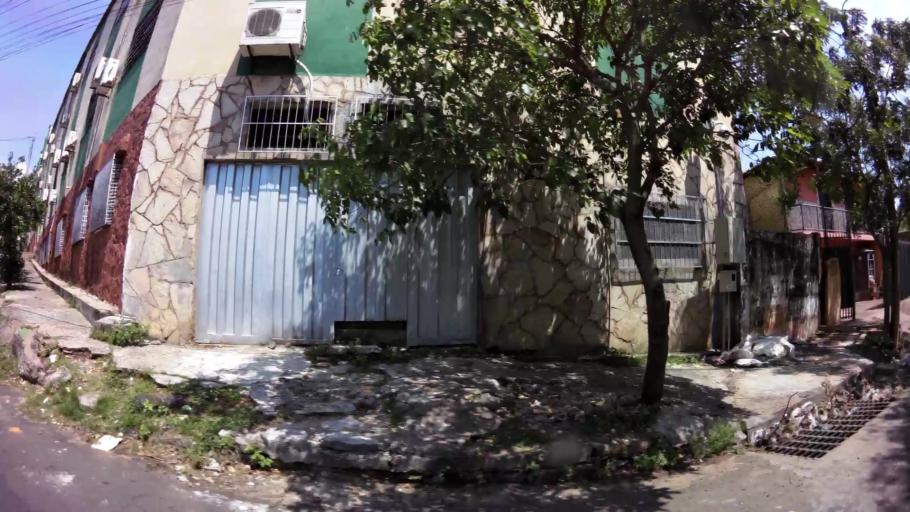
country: PY
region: Asuncion
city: Asuncion
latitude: -25.2804
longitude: -57.6469
